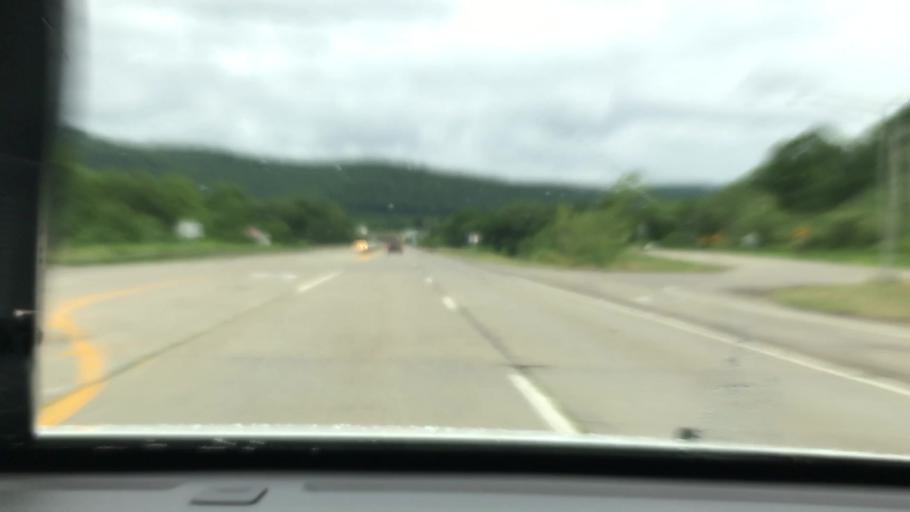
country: US
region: New York
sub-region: Cattaraugus County
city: Salamanca
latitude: 42.0833
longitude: -78.6351
